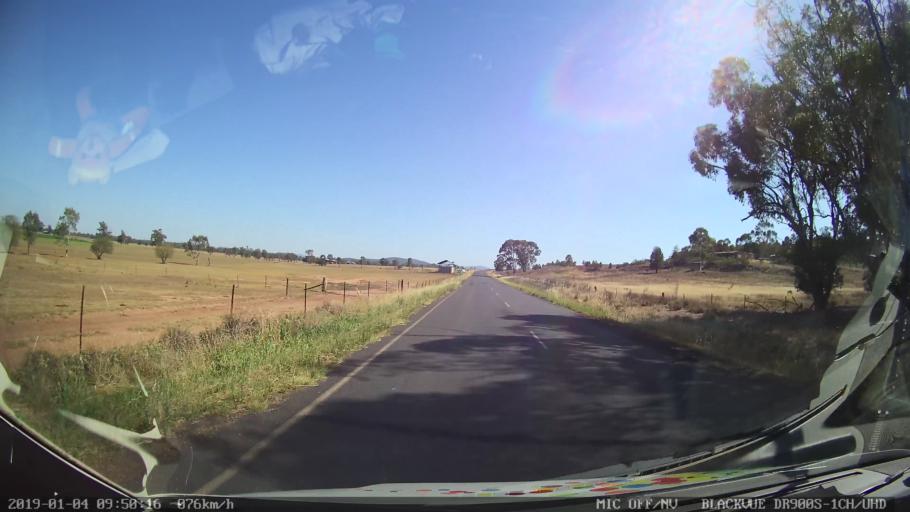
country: AU
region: New South Wales
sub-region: Cabonne
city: Canowindra
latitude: -33.5862
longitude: 148.4148
